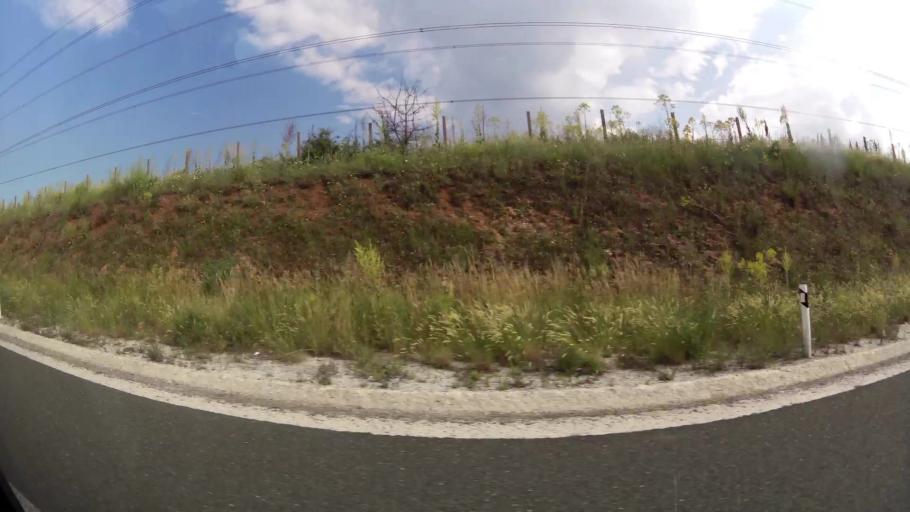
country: GR
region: West Macedonia
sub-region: Nomos Kozanis
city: Kleitos
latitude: 40.3639
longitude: 21.8599
